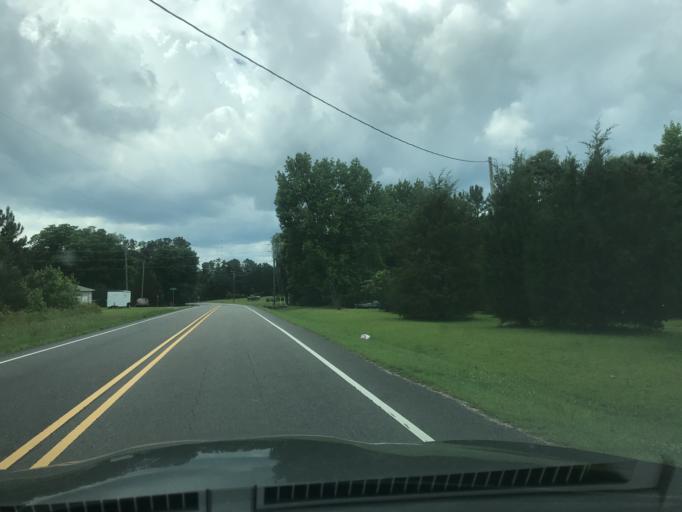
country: US
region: North Carolina
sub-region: Wake County
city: Knightdale
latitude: 35.8341
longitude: -78.4716
